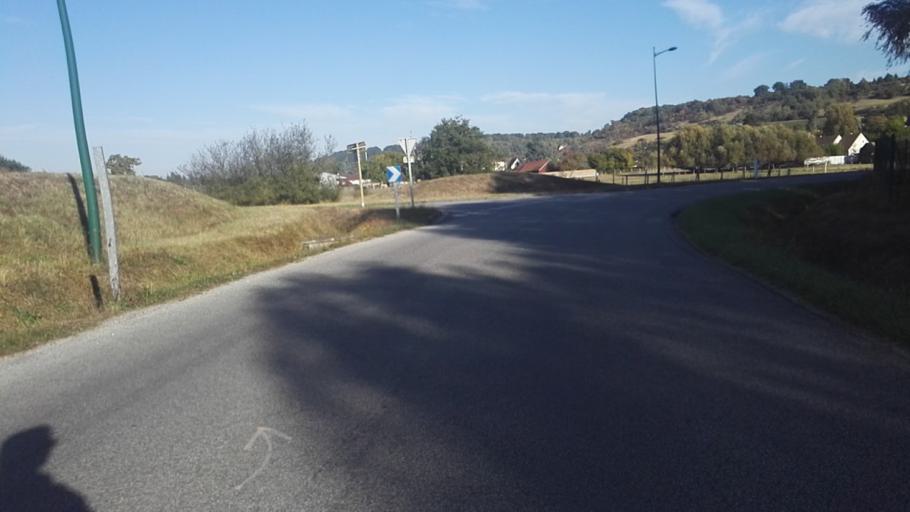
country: FR
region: Haute-Normandie
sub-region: Departement de l'Eure
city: Menilles
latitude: 49.0277
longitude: 1.3686
